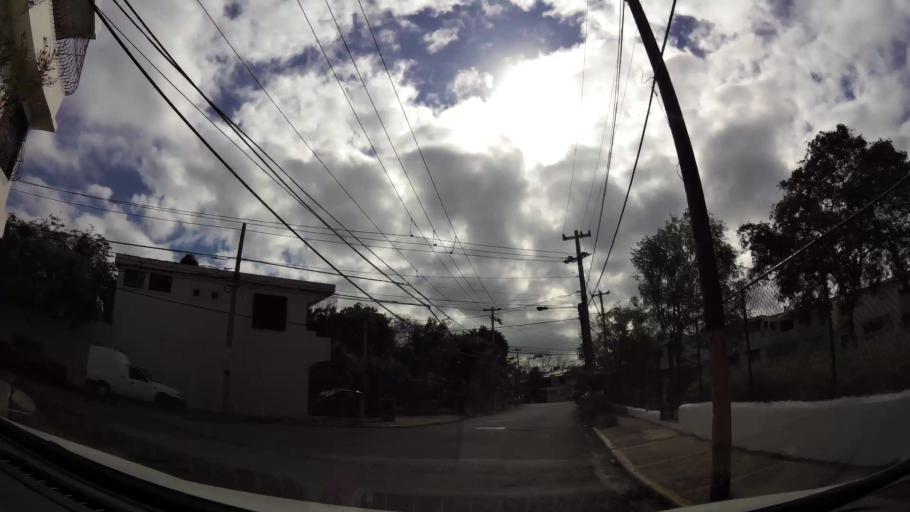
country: DO
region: Nacional
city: Bella Vista
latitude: 18.4455
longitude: -69.9299
